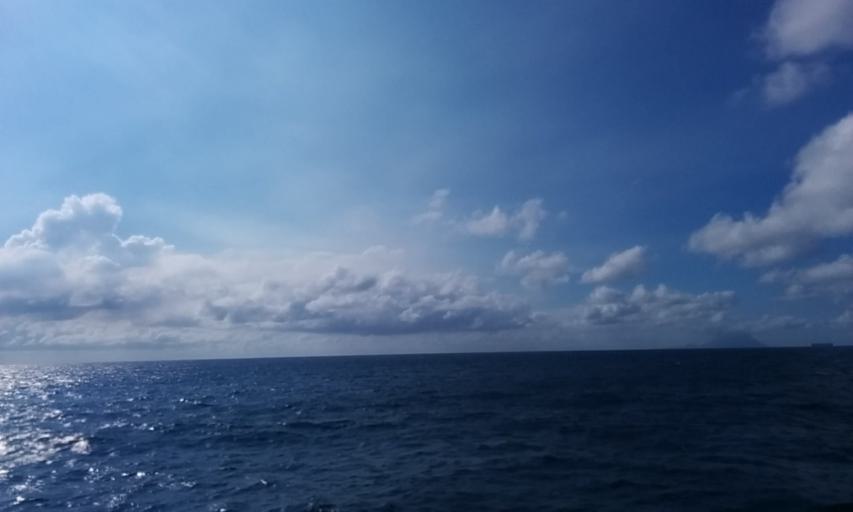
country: JP
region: Kagoshima
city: Nishinoomote
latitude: 30.6683
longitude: 130.6014
